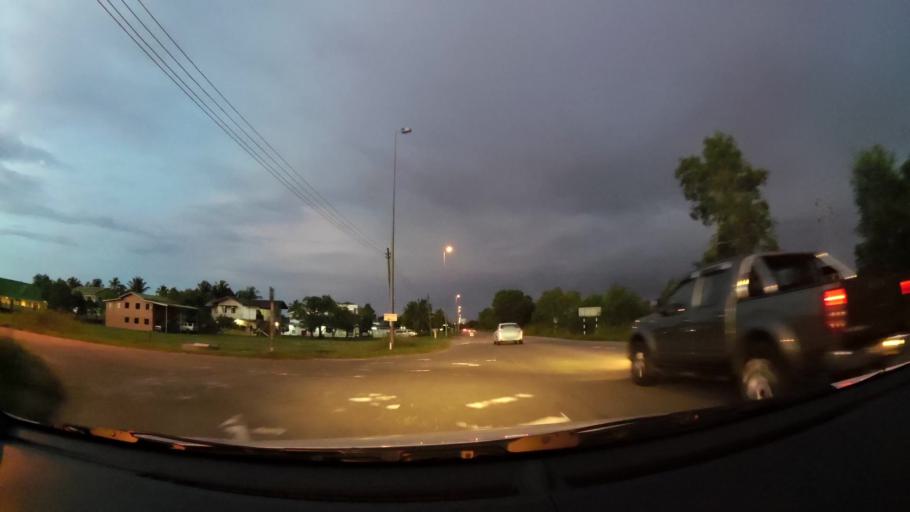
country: BN
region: Belait
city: Seria
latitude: 4.6510
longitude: 114.4217
